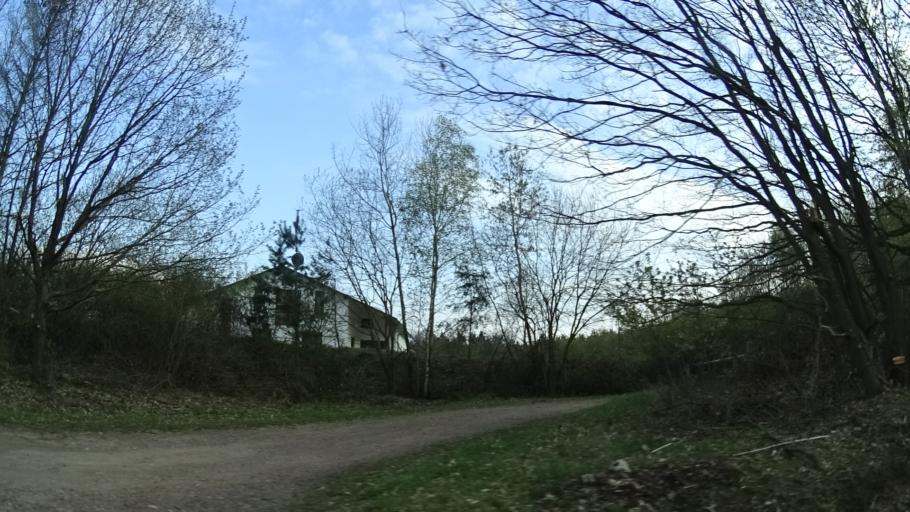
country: DE
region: Rheinland-Pfalz
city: Mandel
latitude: 49.8528
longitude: 7.7539
